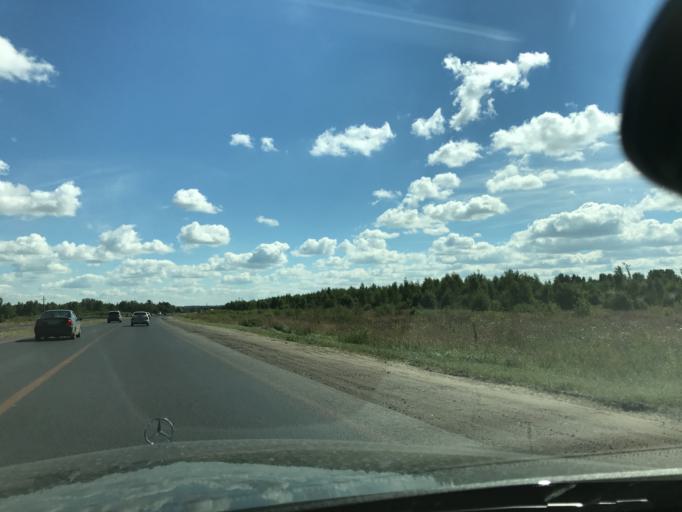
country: RU
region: Nizjnij Novgorod
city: Gorbatovka
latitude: 56.2337
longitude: 43.7407
